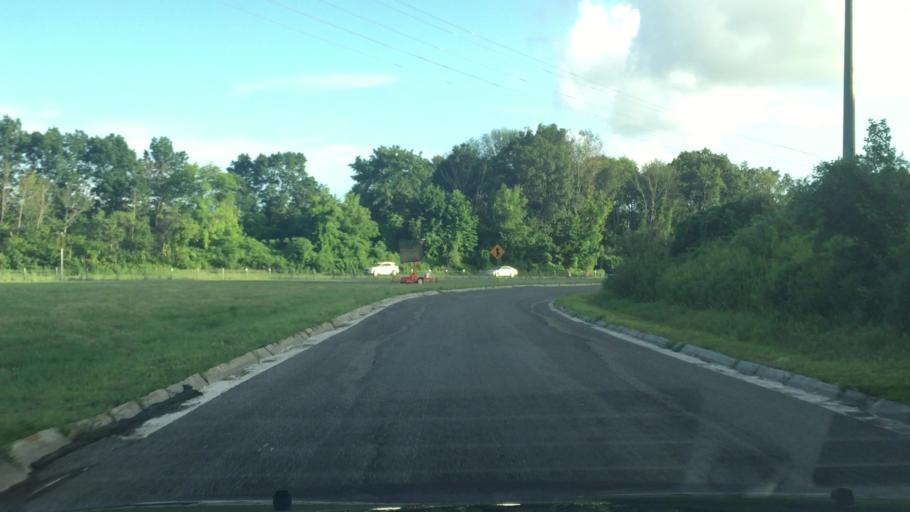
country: US
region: Massachusetts
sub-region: Essex County
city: Methuen
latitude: 42.7418
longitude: -71.1721
